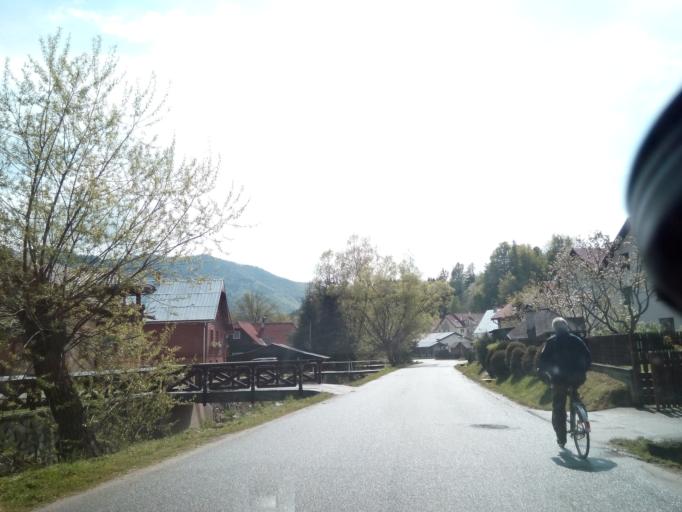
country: SK
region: Zilinsky
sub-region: Okres Zilina
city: Terchova
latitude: 49.2685
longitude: 19.0366
